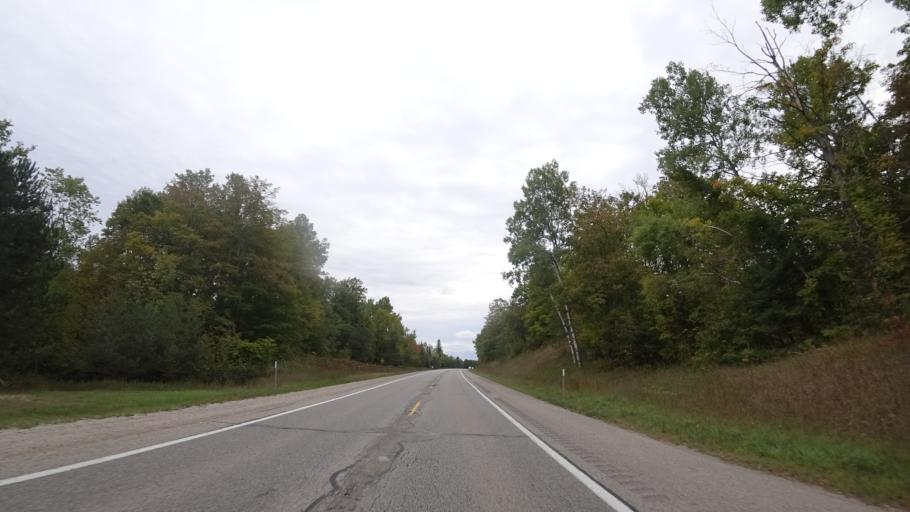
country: US
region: Michigan
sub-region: Charlevoix County
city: Boyne City
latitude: 45.2391
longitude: -84.9166
